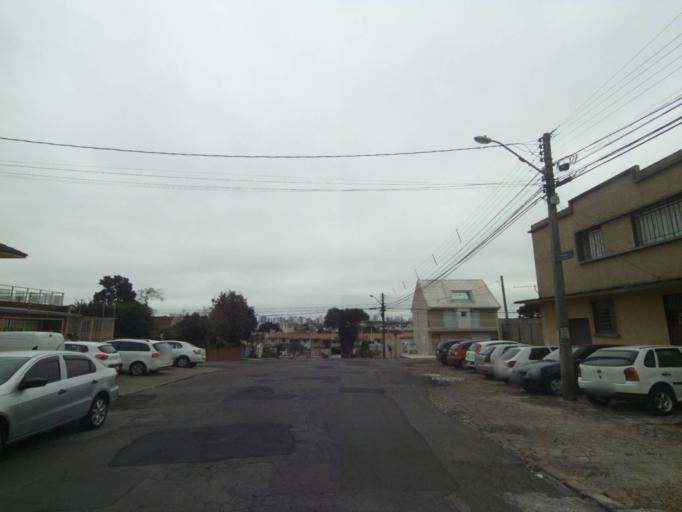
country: BR
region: Parana
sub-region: Curitiba
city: Curitiba
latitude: -25.4734
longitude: -49.2725
